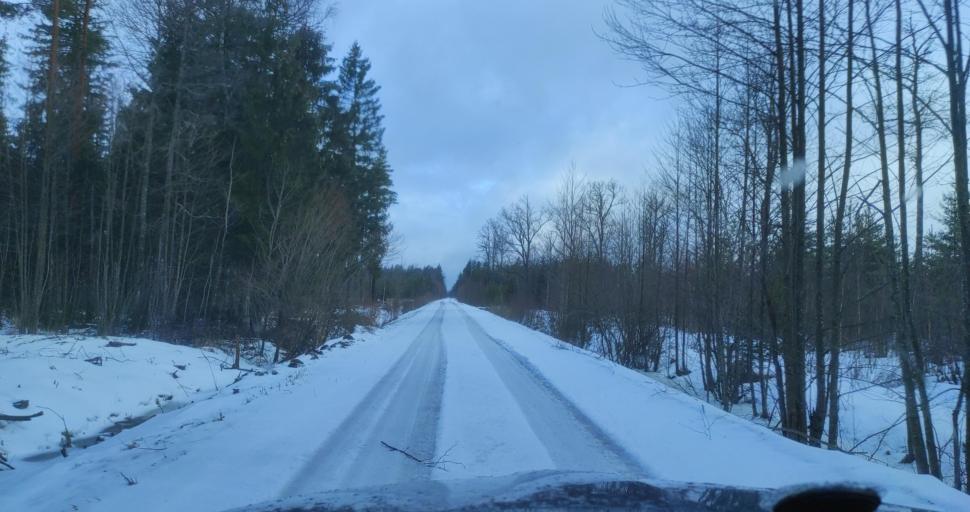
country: LV
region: Dundaga
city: Dundaga
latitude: 57.4081
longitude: 22.0887
